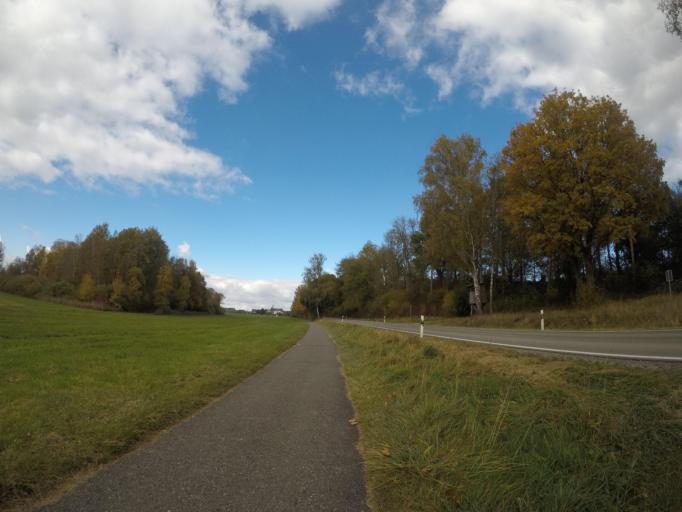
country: DE
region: Baden-Wuerttemberg
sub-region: Tuebingen Region
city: Seekirch
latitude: 48.0963
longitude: 9.6491
